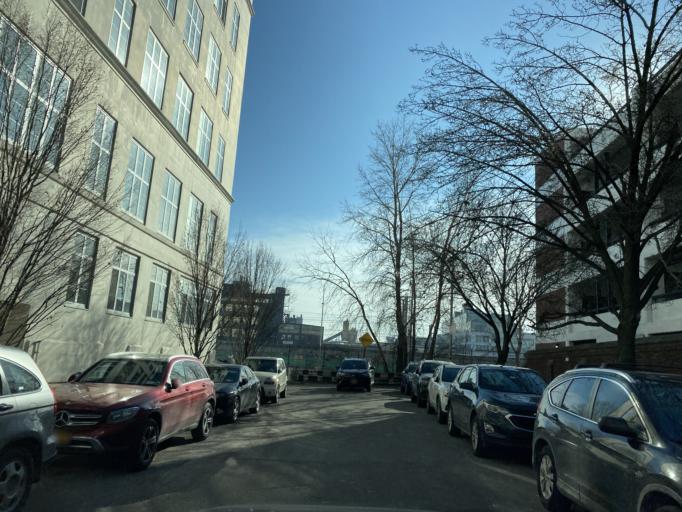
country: US
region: New York
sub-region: Queens County
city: Long Island City
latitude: 40.7455
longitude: -73.9421
